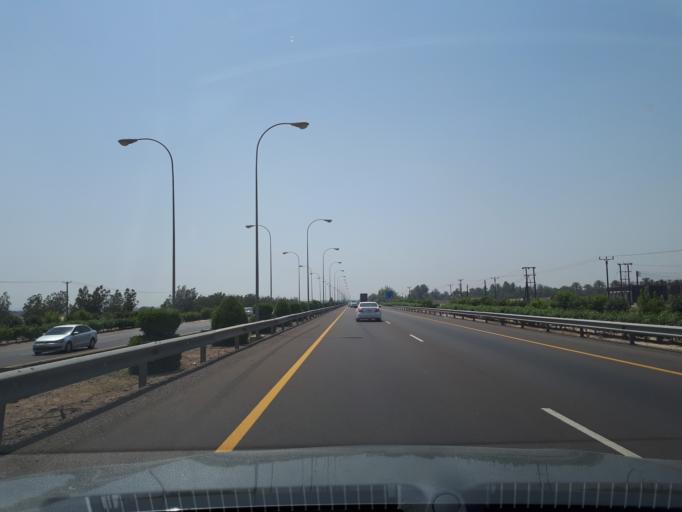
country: OM
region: Al Batinah
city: Al Sohar
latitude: 24.4042
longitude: 56.6568
